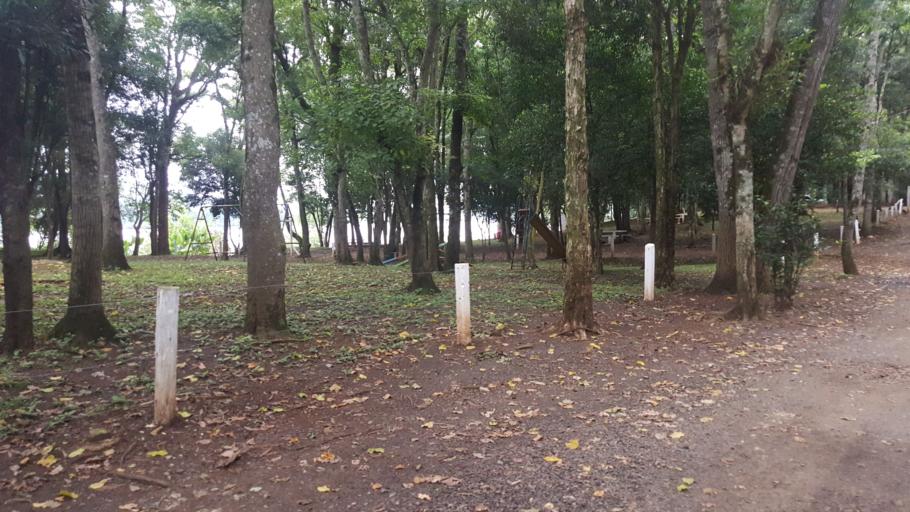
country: BR
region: Rio Grande do Sul
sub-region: Frederico Westphalen
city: Frederico Westphalen
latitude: -27.0886
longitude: -53.3764
